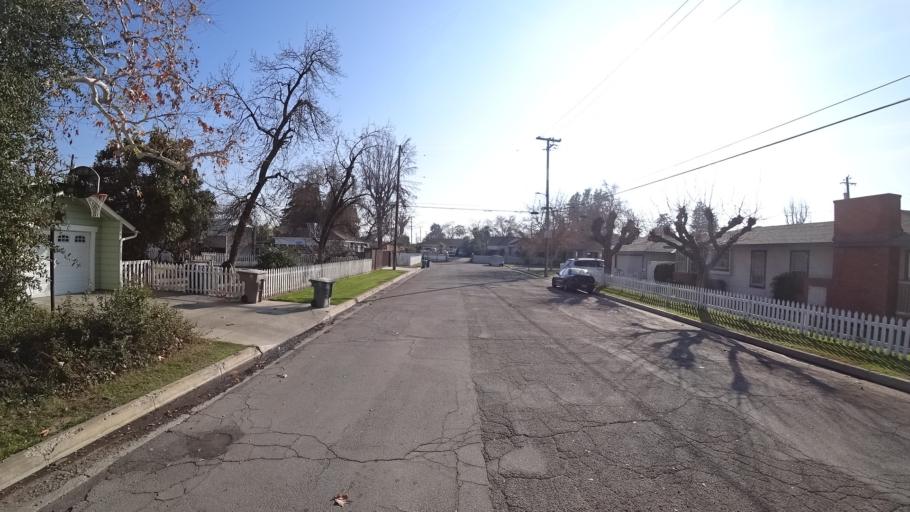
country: US
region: California
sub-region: Kern County
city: Bakersfield
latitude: 35.3579
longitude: -119.0317
